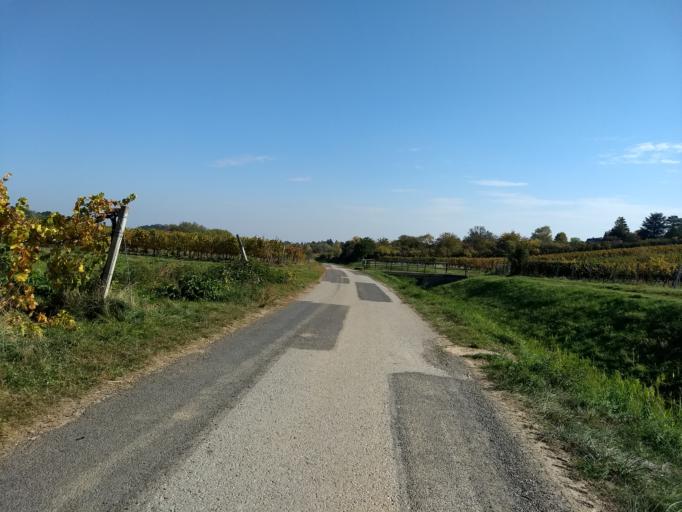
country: AT
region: Lower Austria
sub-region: Politischer Bezirk Modling
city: Perchtoldsdorf
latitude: 48.1102
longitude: 16.2515
